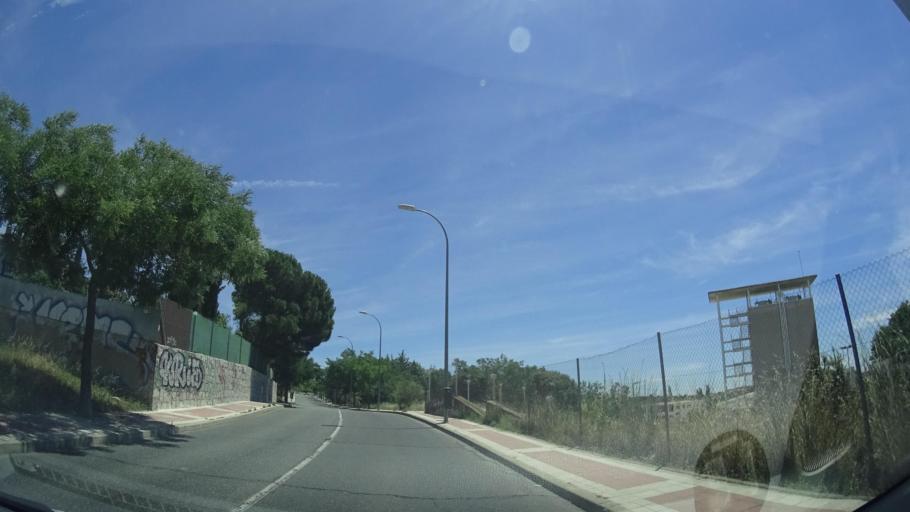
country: ES
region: Madrid
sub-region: Provincia de Madrid
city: Collado-Villalba
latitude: 40.6205
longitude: -3.9948
